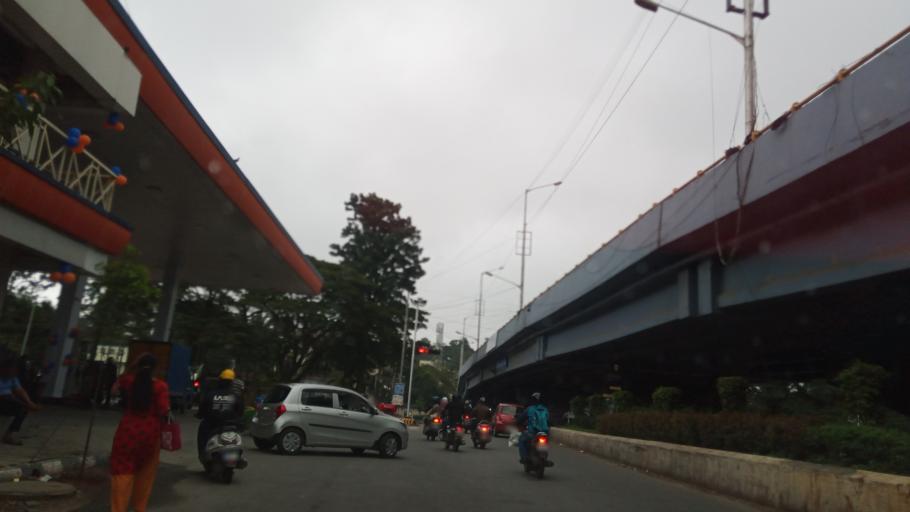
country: IN
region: Karnataka
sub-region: Bangalore Urban
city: Bangalore
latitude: 12.9220
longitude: 77.5597
